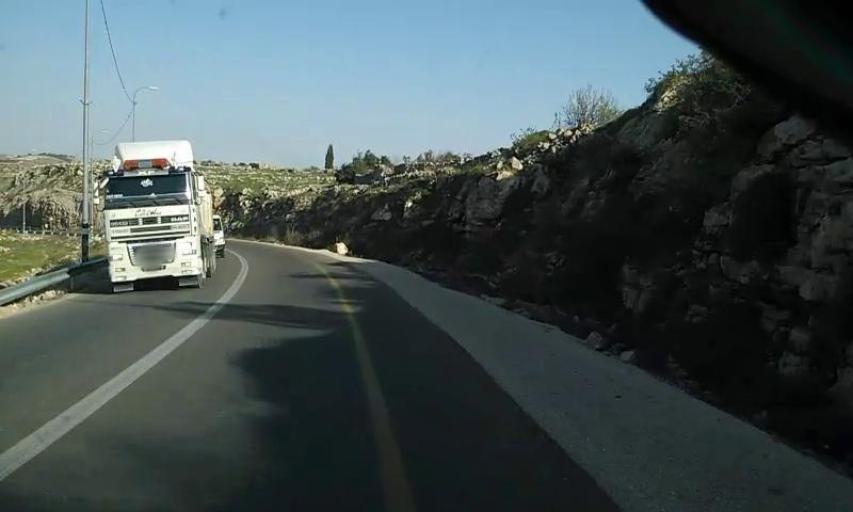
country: PS
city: Khallat ad Dar
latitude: 31.5009
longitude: 35.1127
